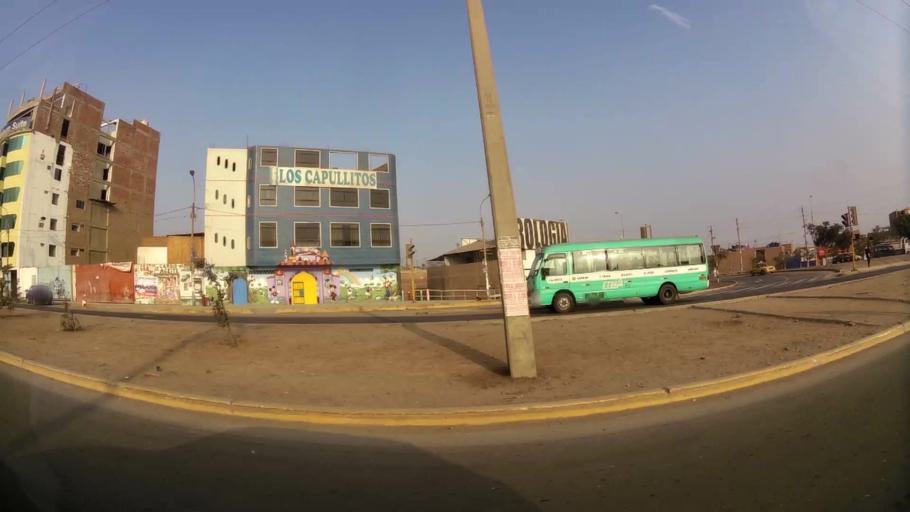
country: PE
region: Lima
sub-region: Lima
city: Independencia
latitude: -11.9809
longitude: -77.0958
